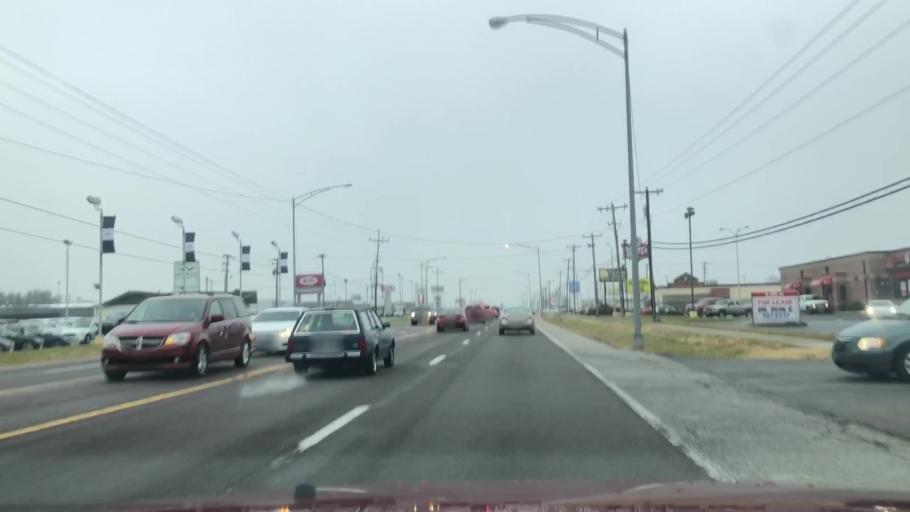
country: US
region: Missouri
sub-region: Greene County
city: Springfield
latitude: 37.1483
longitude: -93.2958
